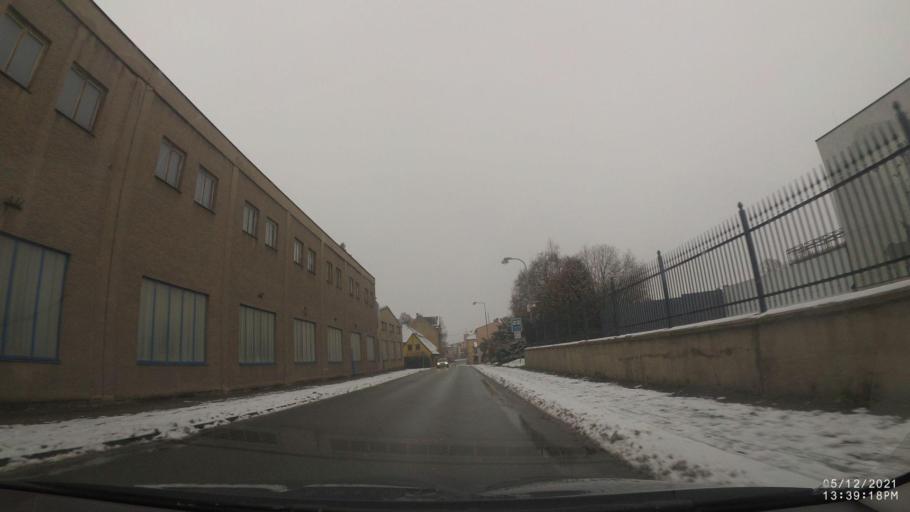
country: CZ
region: Kralovehradecky
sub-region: Okres Nachod
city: Police nad Metuji
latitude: 50.5336
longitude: 16.2338
